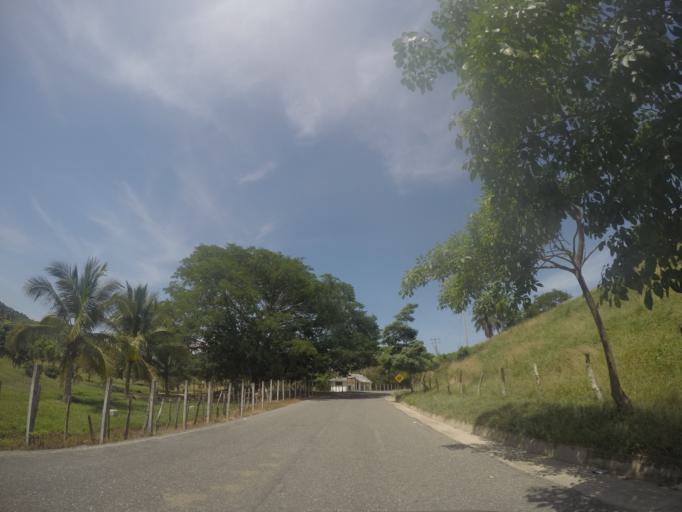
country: MX
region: Oaxaca
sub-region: Villa de Tututepec de Melchor Ocampo
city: Santa Rosa de Lima
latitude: 15.9902
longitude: -97.5420
